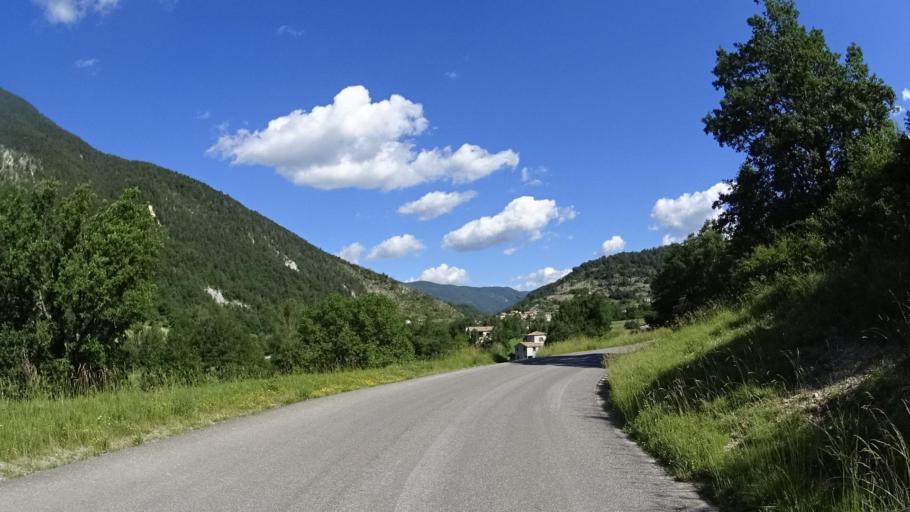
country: FR
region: Provence-Alpes-Cote d'Azur
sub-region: Departement des Alpes-de-Haute-Provence
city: Annot
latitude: 43.9970
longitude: 6.6452
